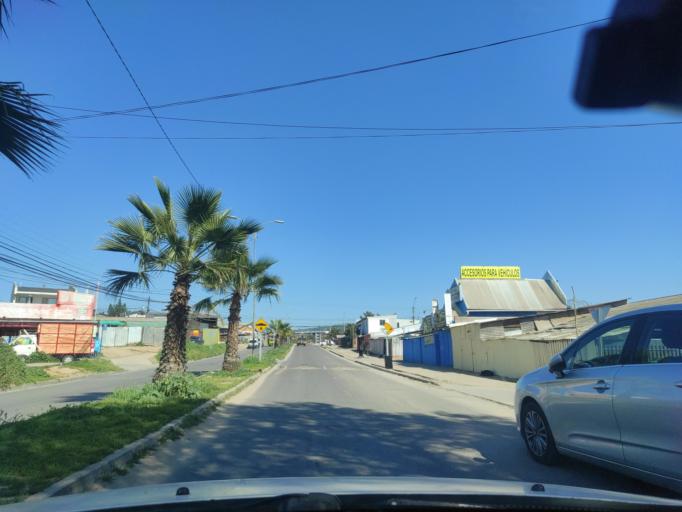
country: CL
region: Valparaiso
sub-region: Provincia de Marga Marga
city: Limache
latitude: -33.0153
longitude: -71.2561
